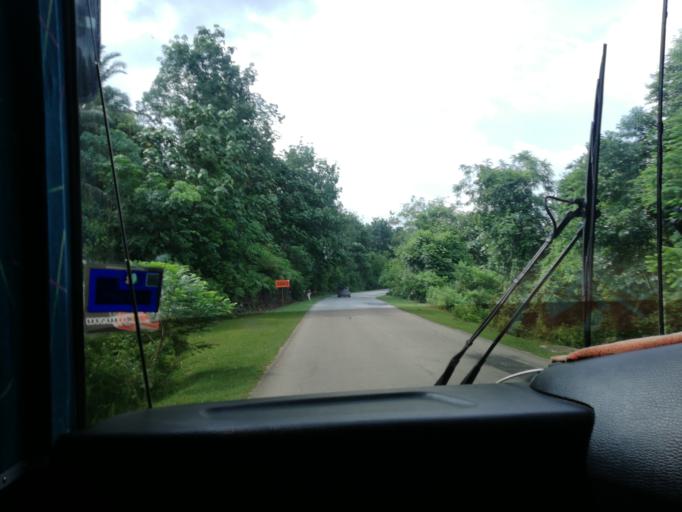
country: MY
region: Kedah
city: Kulim
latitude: 5.3389
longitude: 100.5892
